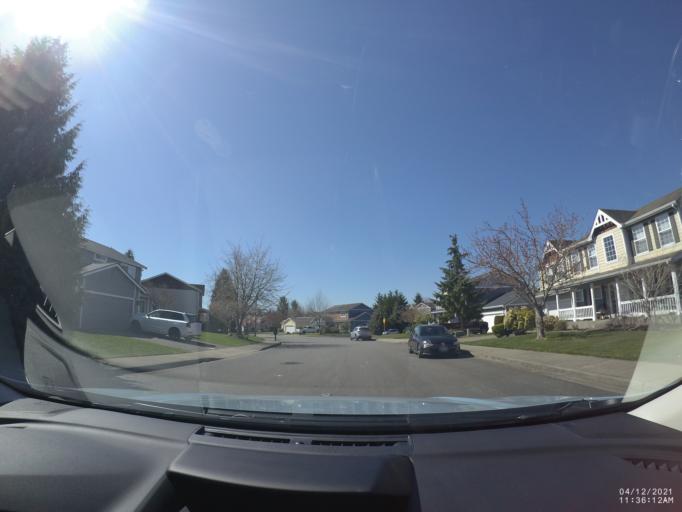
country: US
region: Washington
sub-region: Pierce County
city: McMillin
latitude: 47.1043
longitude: -122.2483
